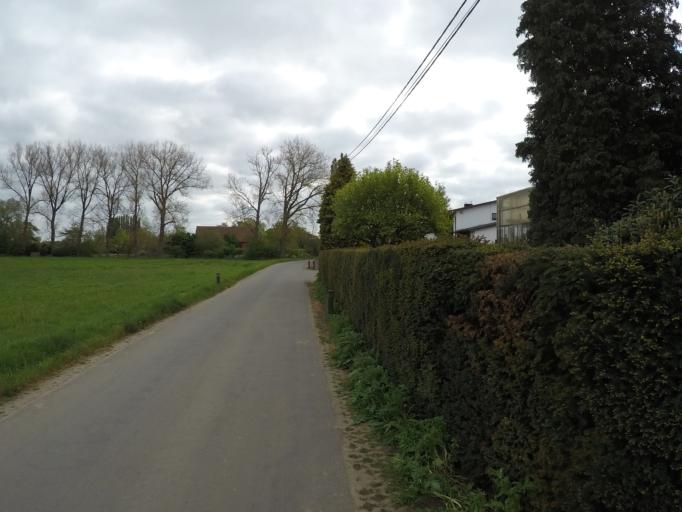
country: BE
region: Flanders
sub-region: Provincie Antwerpen
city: Boechout
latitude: 51.1770
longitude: 4.4911
